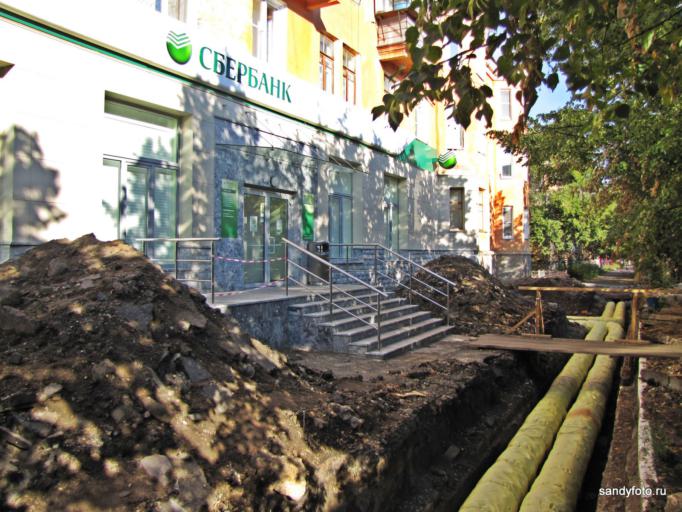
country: RU
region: Chelyabinsk
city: Troitsk
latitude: 54.0453
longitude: 61.6296
